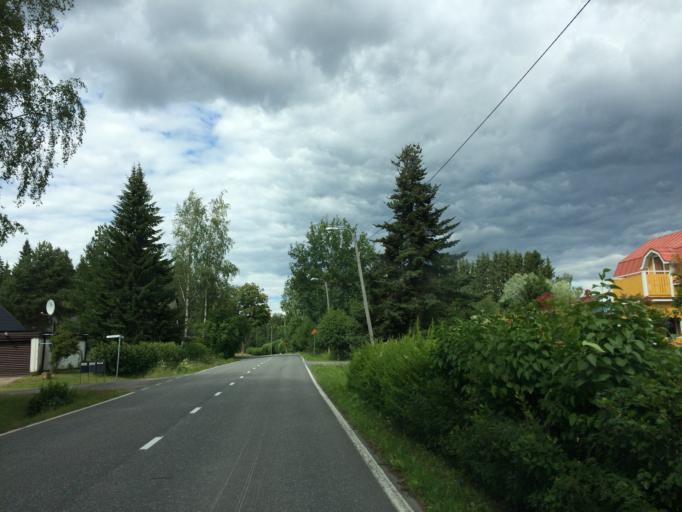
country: FI
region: Haeme
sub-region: Haemeenlinna
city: Tervakoski
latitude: 60.8237
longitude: 24.6220
